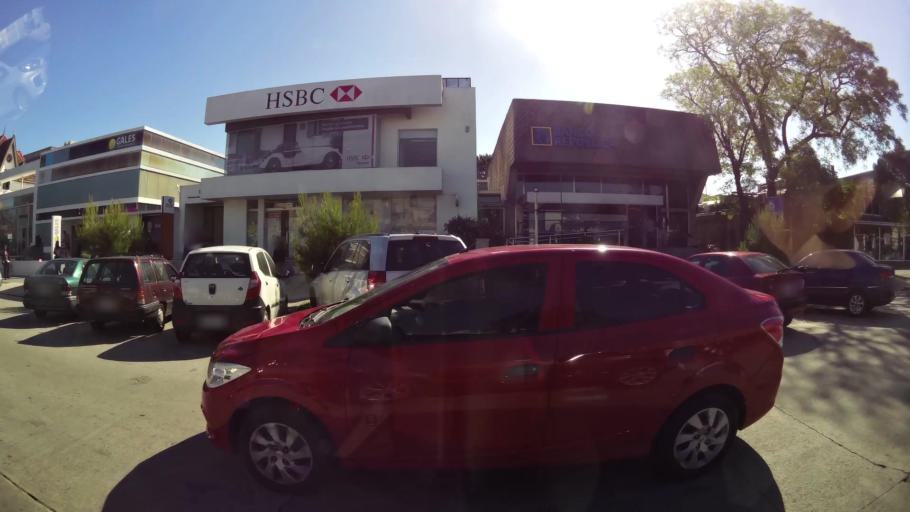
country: UY
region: Canelones
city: Paso de Carrasco
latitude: -34.8881
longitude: -56.0577
